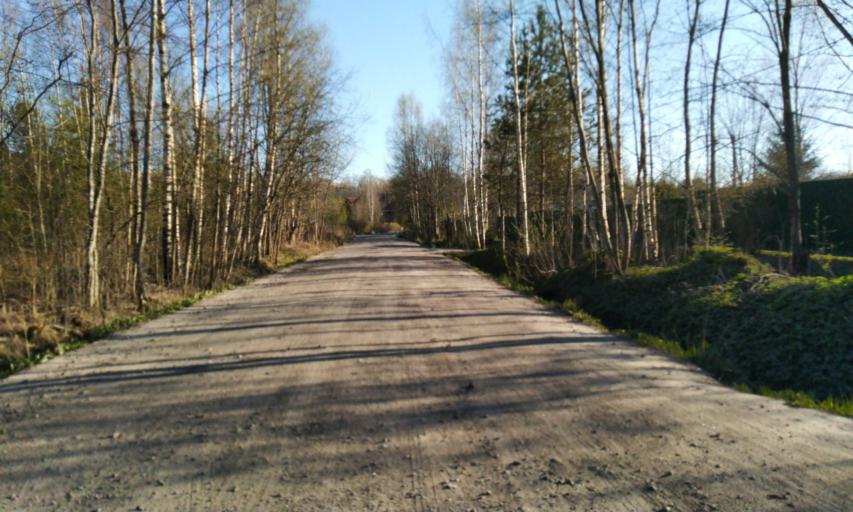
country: RU
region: Leningrad
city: Toksovo
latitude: 60.1517
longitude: 30.5823
